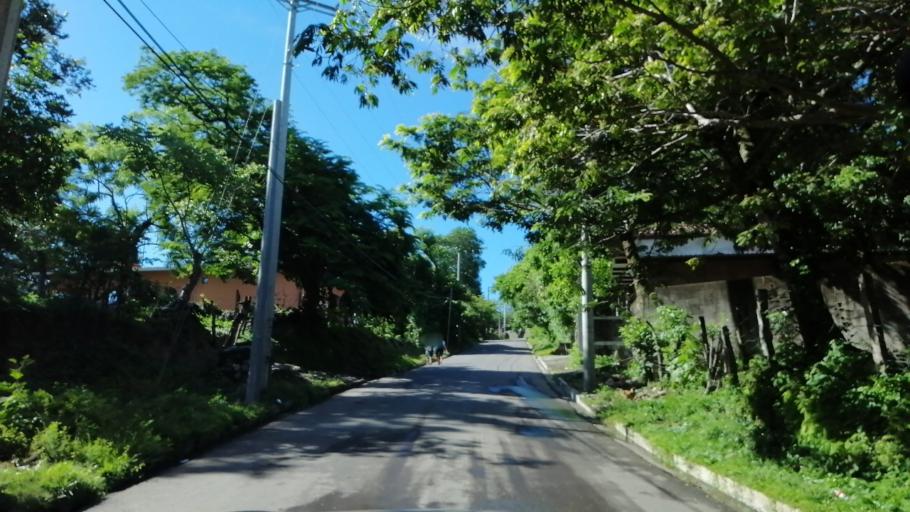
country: SV
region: Morazan
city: Corinto
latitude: 13.8051
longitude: -87.9675
